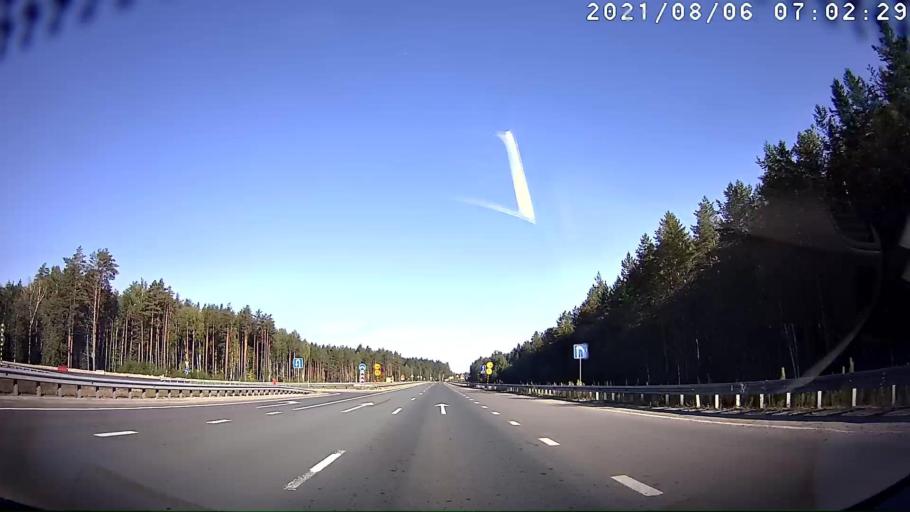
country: RU
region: Mariy-El
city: Yoshkar-Ola
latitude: 56.5345
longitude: 47.9957
